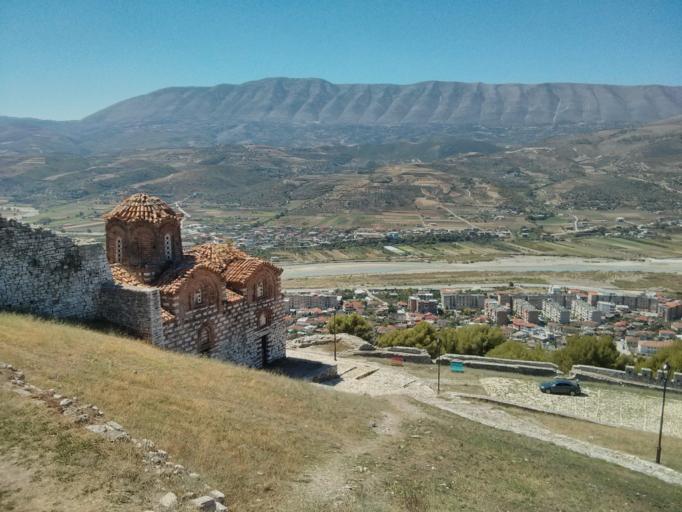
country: AL
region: Berat
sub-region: Rrethi i Beratit
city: Berat
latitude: 40.7081
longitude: 19.9448
